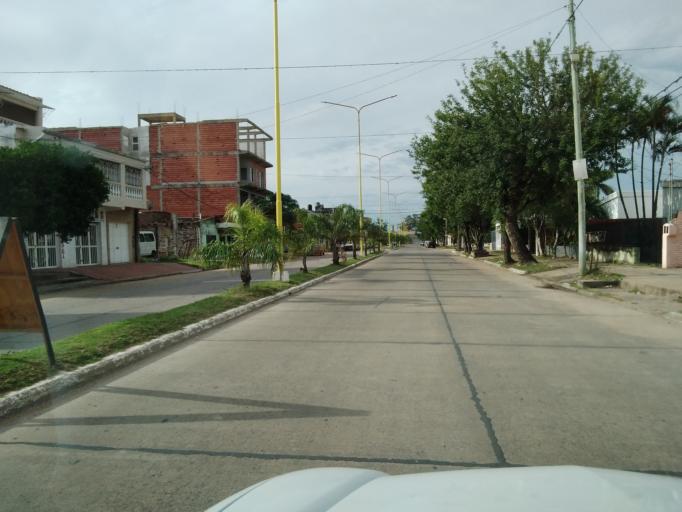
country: AR
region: Corrientes
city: Corrientes
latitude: -27.4642
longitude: -58.7883
